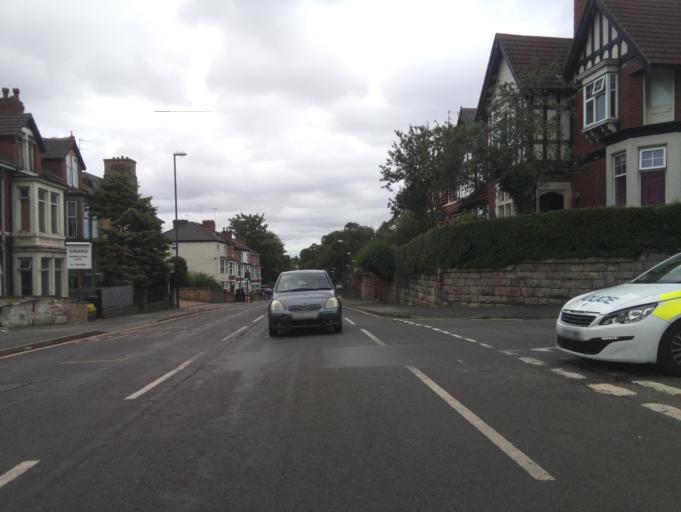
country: GB
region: England
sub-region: Derby
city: Derby
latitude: 52.9127
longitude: -1.4868
